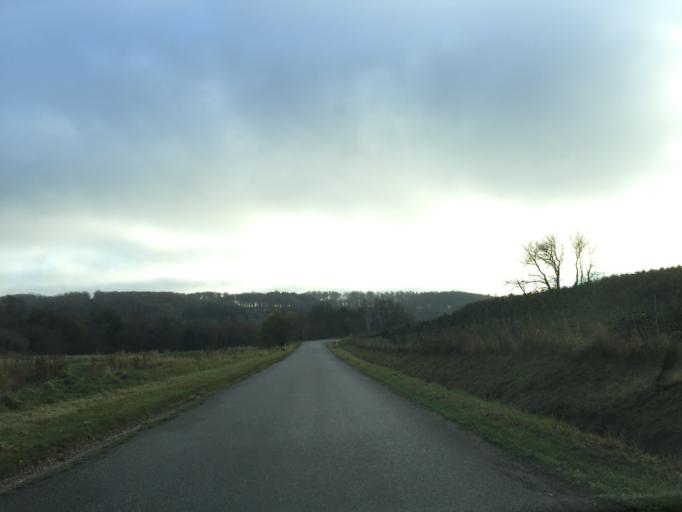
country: DK
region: Central Jutland
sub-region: Skanderborg Kommune
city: Ry
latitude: 56.1672
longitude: 9.7739
